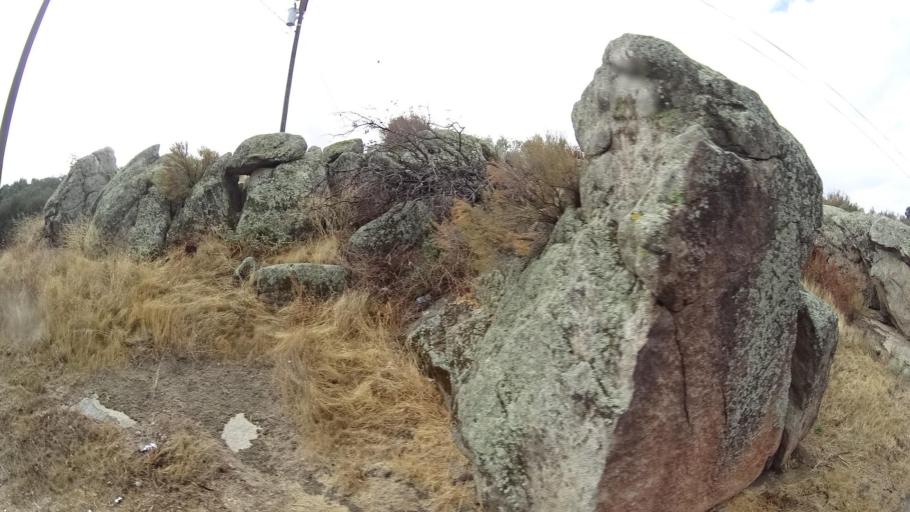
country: US
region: California
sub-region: San Diego County
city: Campo
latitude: 32.6082
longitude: -116.4748
